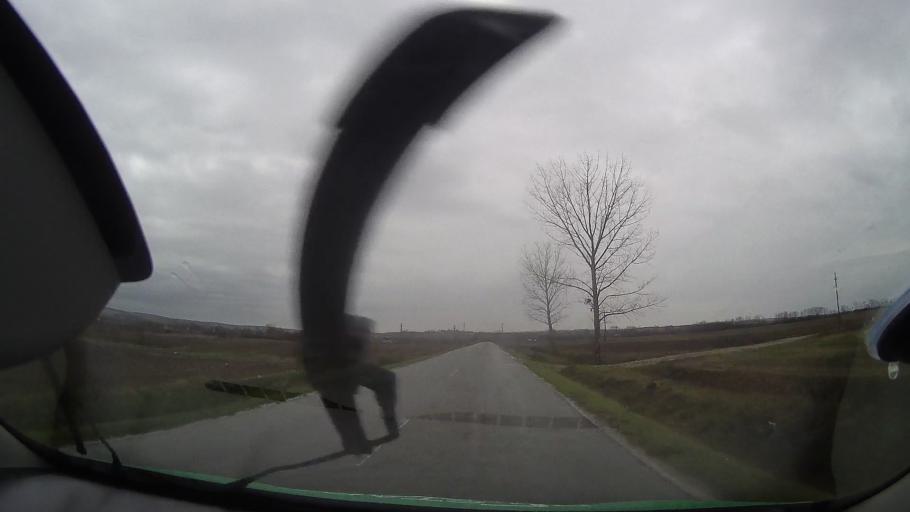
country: RO
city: Capalna
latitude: 46.7120
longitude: 22.0618
